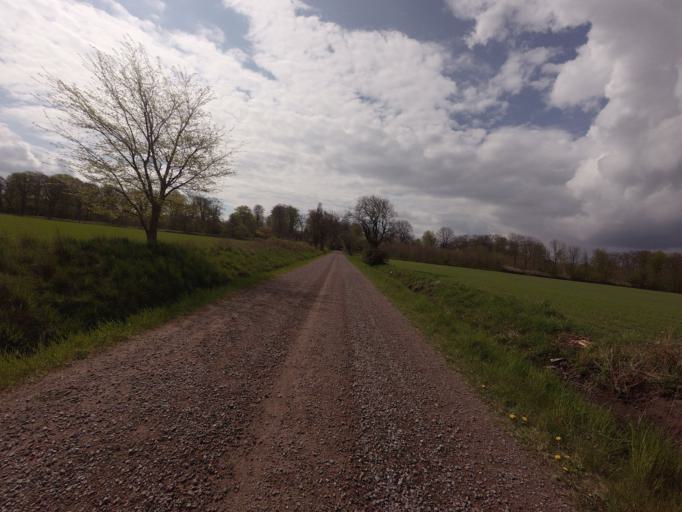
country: DK
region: Capital Region
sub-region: Helsingor Kommune
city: Helsingor
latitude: 56.1124
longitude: 12.6293
